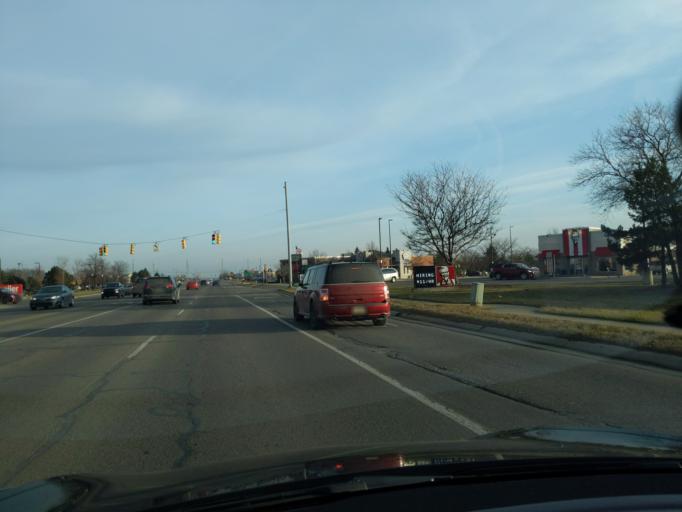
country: US
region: Michigan
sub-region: Livingston County
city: Howell
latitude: 42.5886
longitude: -83.8793
